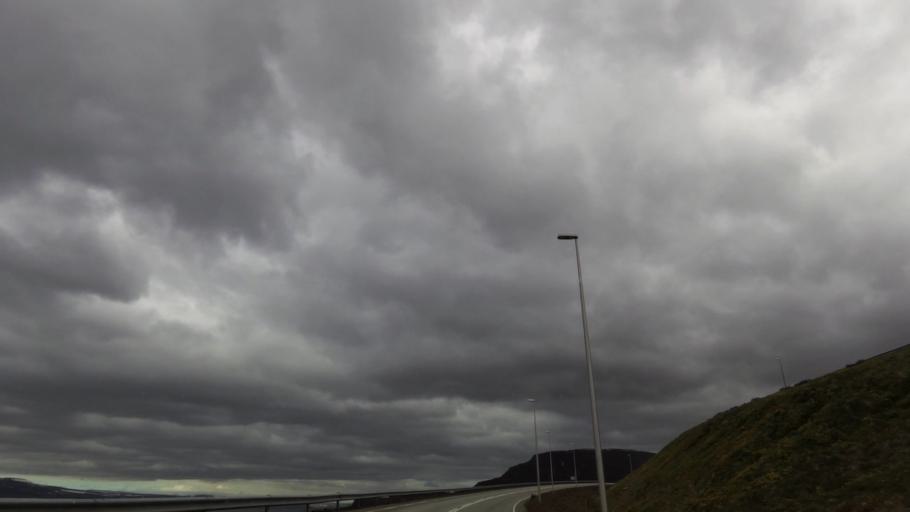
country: IS
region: Westfjords
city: Isafjoerdur
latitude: 66.1088
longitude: -23.1149
